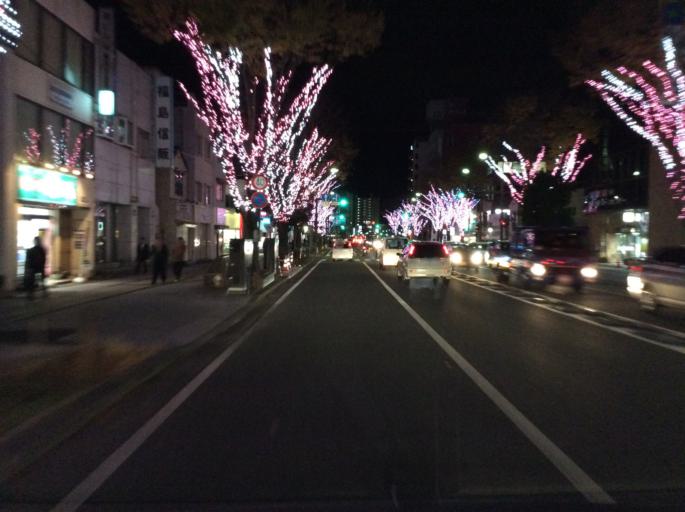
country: JP
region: Fukushima
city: Iwaki
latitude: 37.0557
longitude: 140.8927
